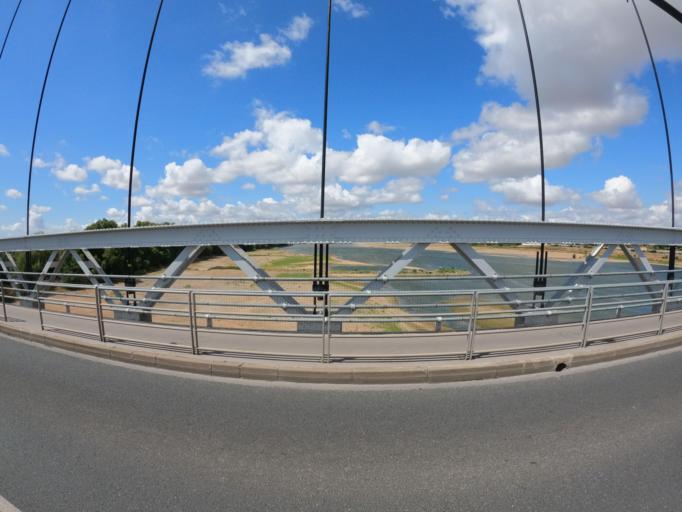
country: FR
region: Pays de la Loire
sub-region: Departement de la Loire-Atlantique
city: Ancenis
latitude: 47.3613
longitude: -1.1770
